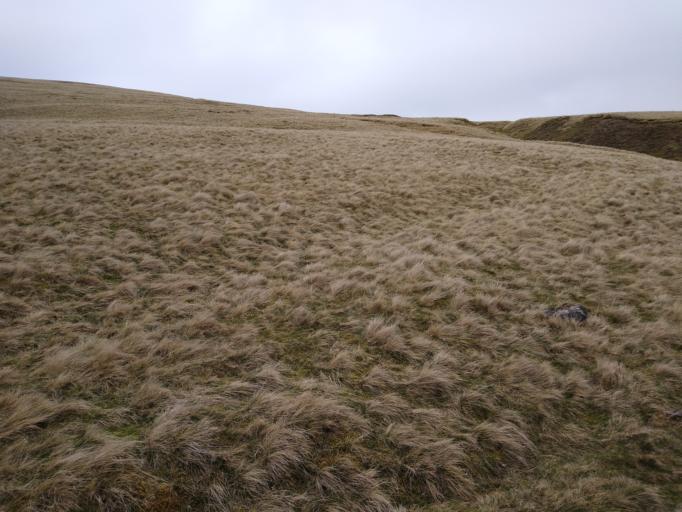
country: GB
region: England
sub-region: Cumbria
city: Keswick
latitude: 54.7081
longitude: -3.0459
